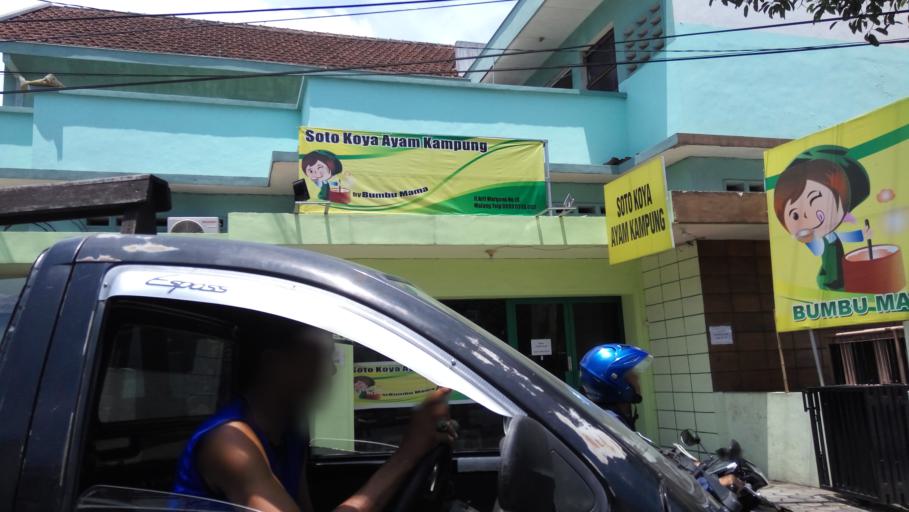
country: ID
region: East Java
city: Malang
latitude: -7.9847
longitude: 112.6254
